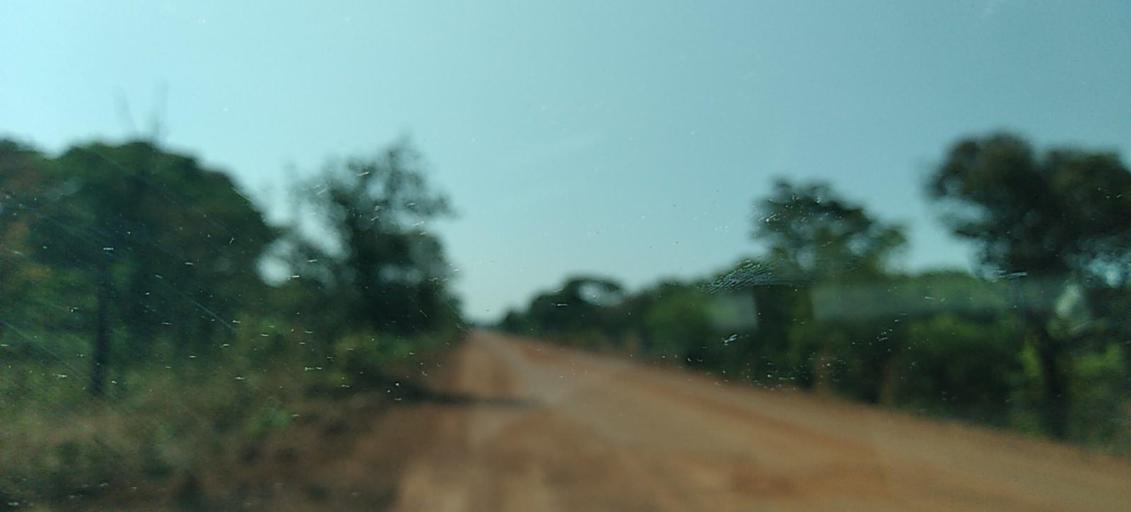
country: ZM
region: North-Western
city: Mwinilunga
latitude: -11.9157
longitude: 25.3073
